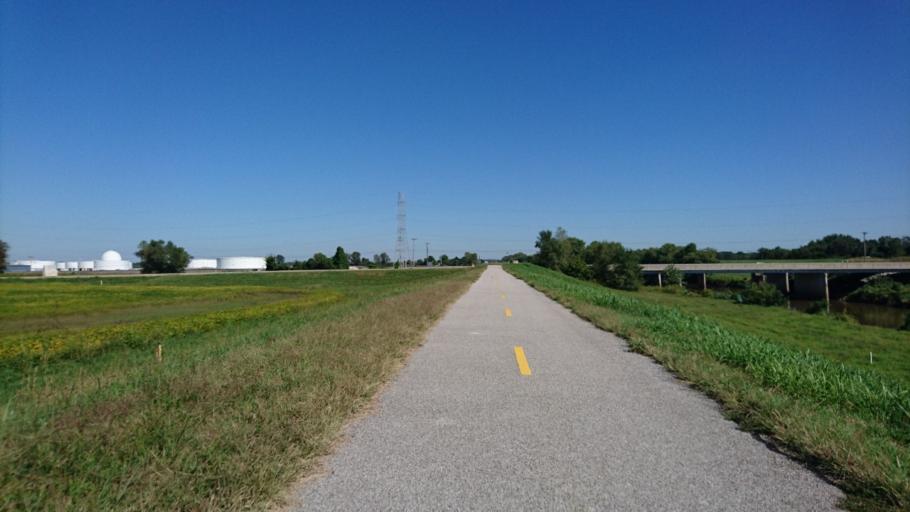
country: US
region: Illinois
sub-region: Madison County
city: Hartford
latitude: 38.8061
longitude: -90.1010
